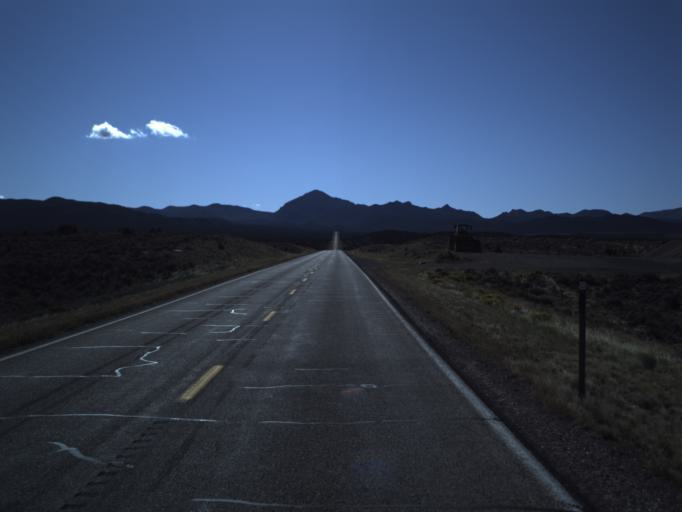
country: US
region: Utah
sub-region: Washington County
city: Enterprise
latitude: 37.6562
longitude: -113.4561
